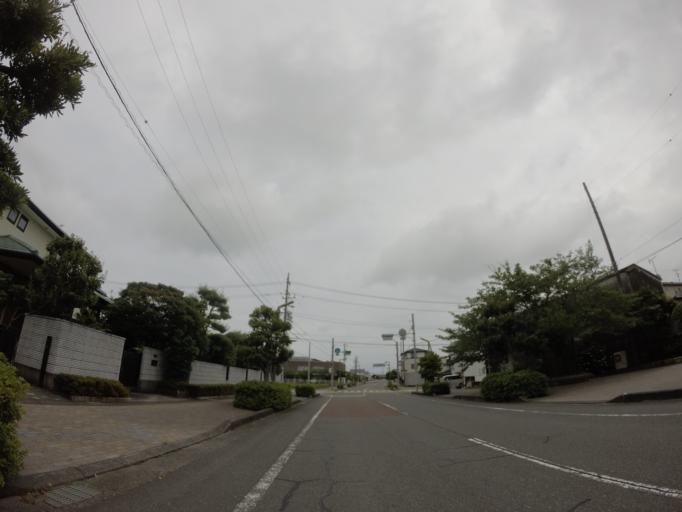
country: JP
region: Shizuoka
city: Sagara
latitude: 34.7375
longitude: 138.2221
